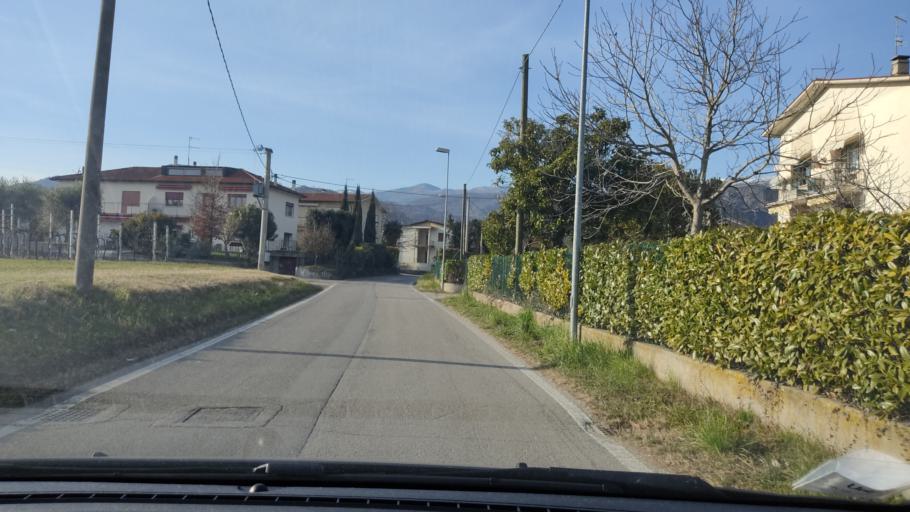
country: IT
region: Veneto
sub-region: Provincia di Treviso
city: Vittorio Veneto
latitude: 45.9677
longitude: 12.3018
